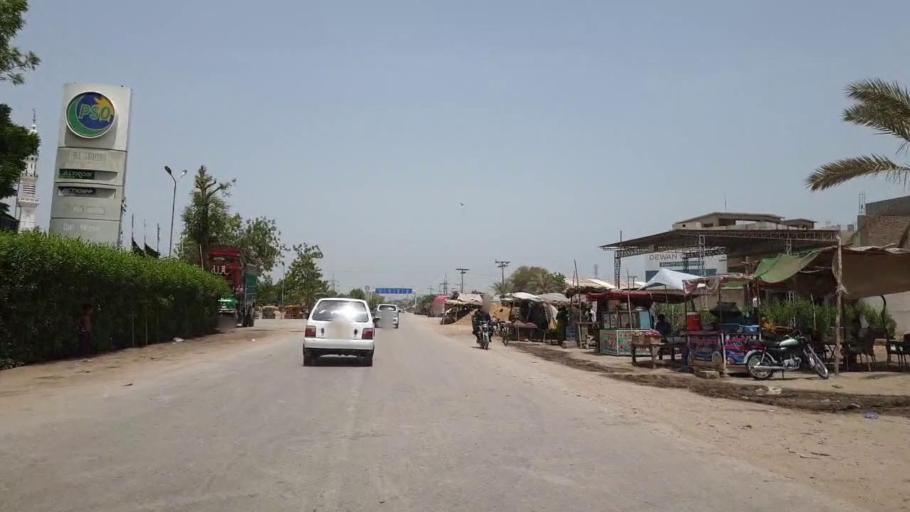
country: PK
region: Sindh
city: Nawabshah
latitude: 26.2474
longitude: 68.4316
